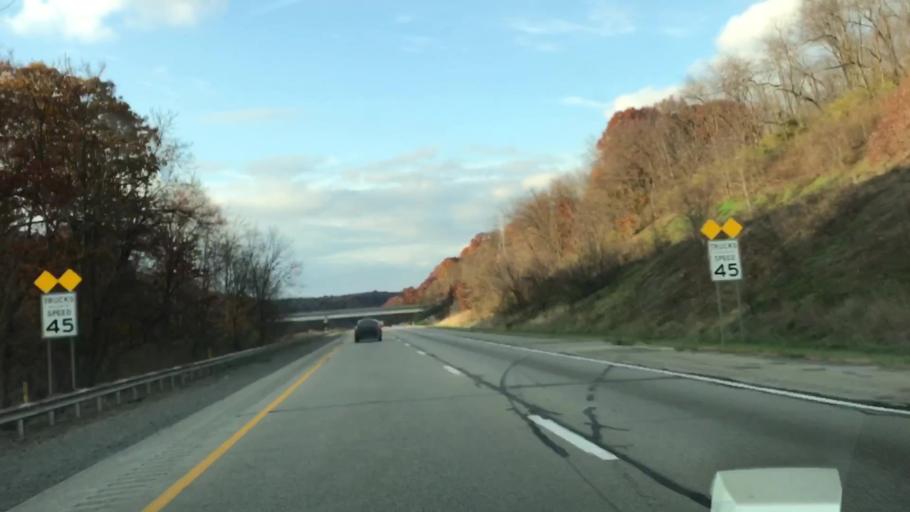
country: US
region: Pennsylvania
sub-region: Allegheny County
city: Emsworth
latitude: 40.4775
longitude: -80.1189
